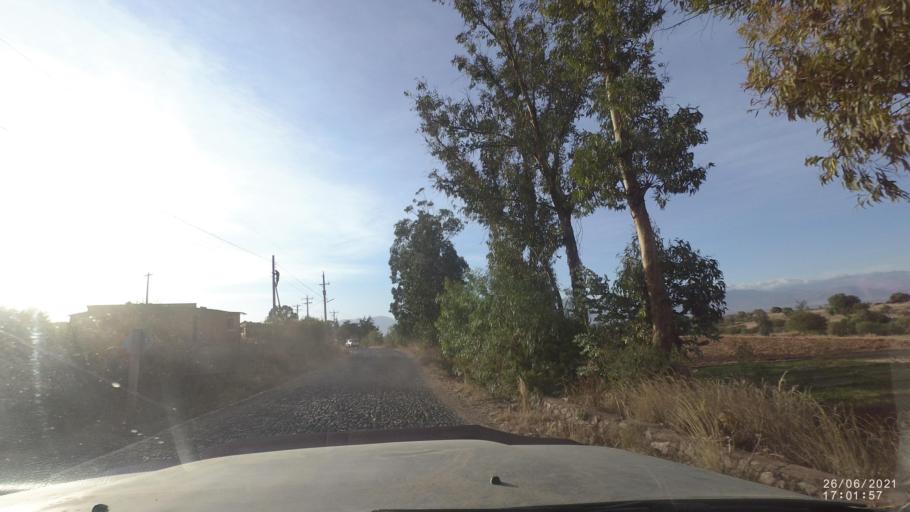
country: BO
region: Cochabamba
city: Cliza
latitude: -17.6570
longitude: -65.9106
